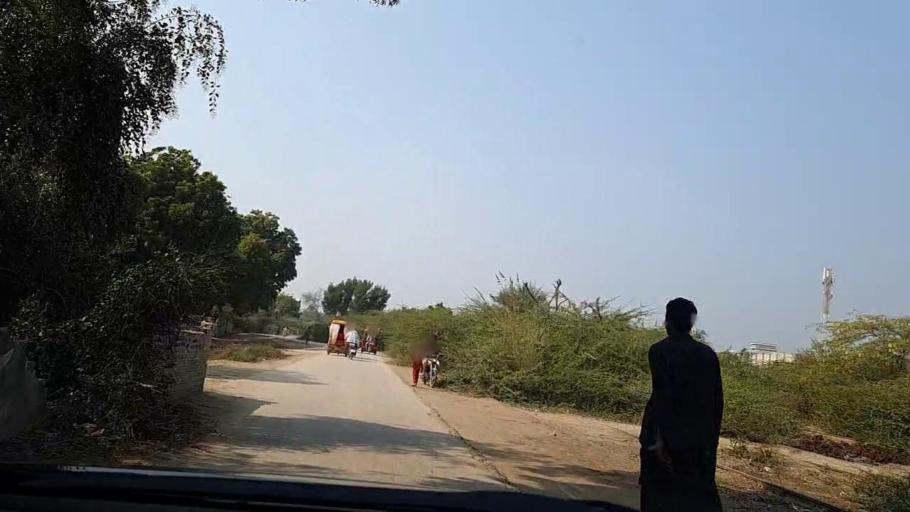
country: PK
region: Sindh
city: Sakrand
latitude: 26.1408
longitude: 68.2769
